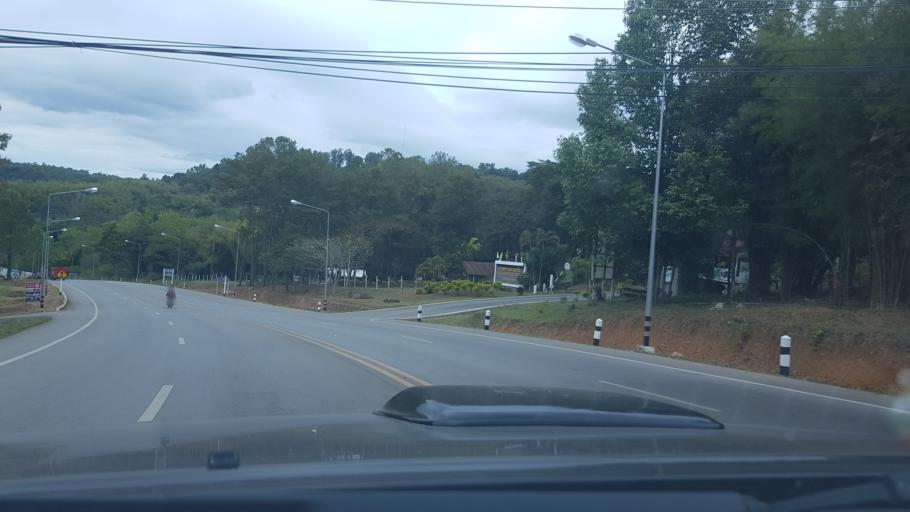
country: TH
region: Phetchabun
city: Khao Kho
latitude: 16.5699
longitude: 100.9923
